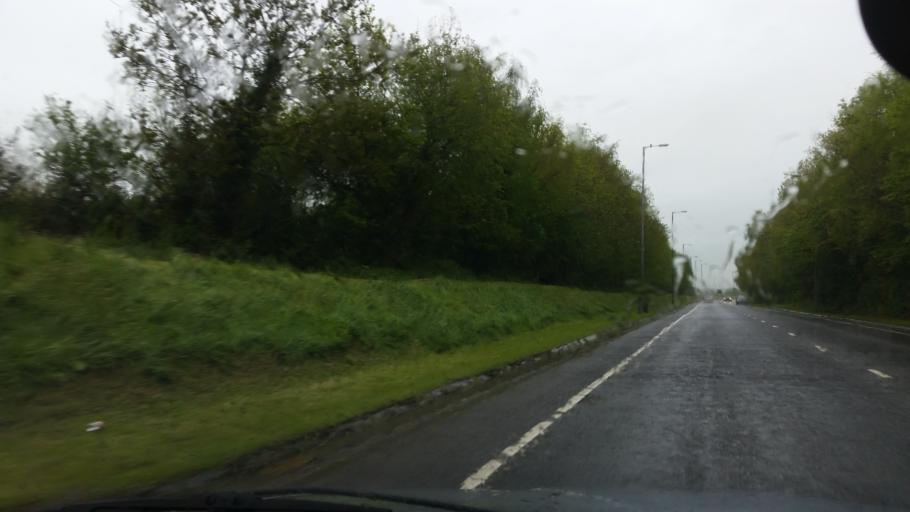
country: GB
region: Northern Ireland
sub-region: Strabane District
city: Strabane
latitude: 54.8350
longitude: -7.4640
